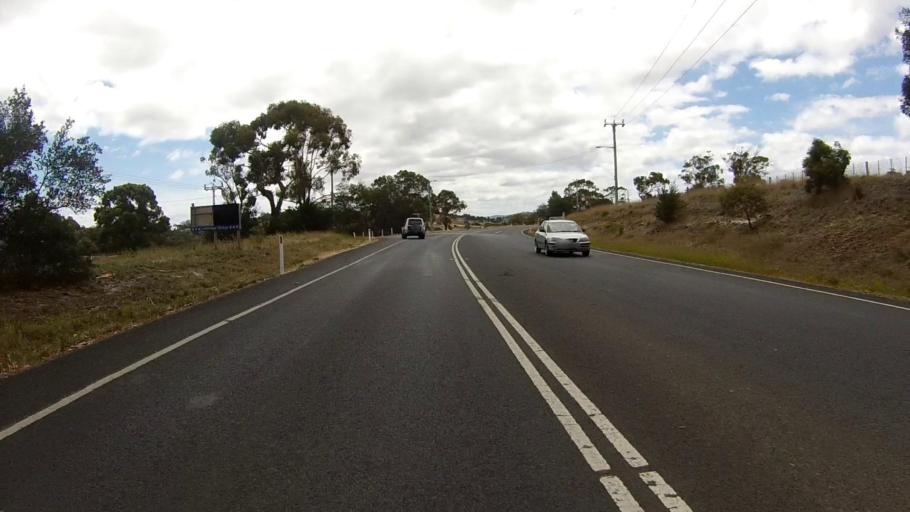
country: AU
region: Tasmania
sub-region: Sorell
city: Sorell
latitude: -42.8418
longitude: 147.6230
